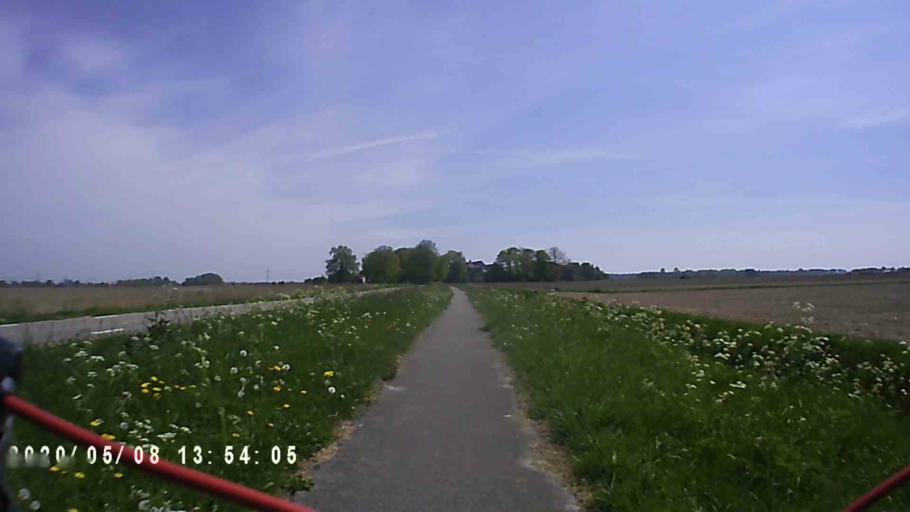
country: NL
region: Groningen
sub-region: Gemeente Appingedam
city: Appingedam
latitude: 53.3376
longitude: 6.7859
